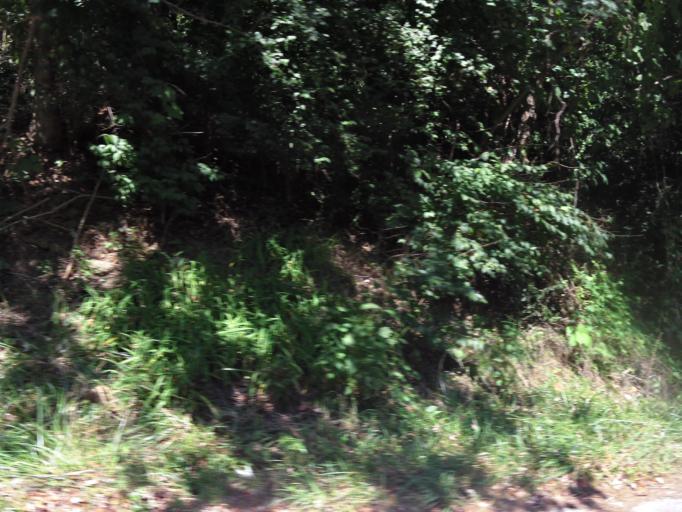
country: US
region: Kentucky
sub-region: Harlan County
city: Harlan
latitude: 36.8569
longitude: -83.3182
